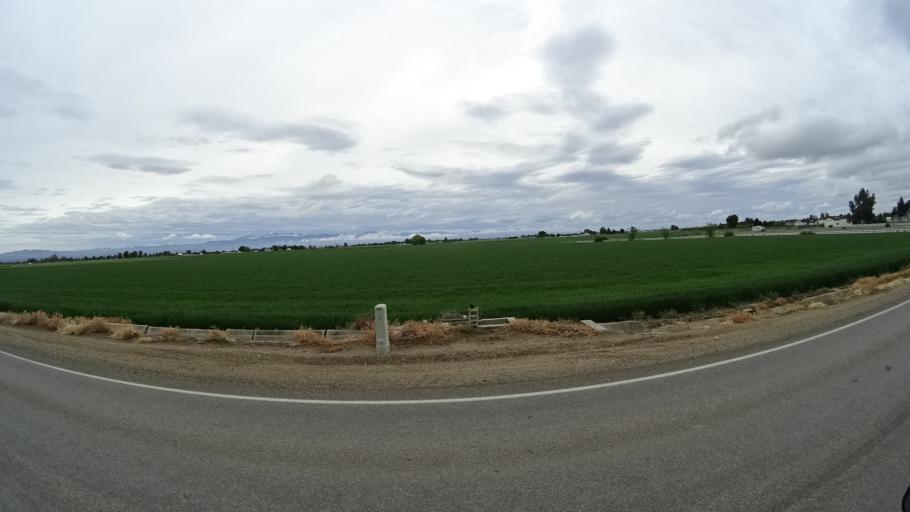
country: US
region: Idaho
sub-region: Ada County
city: Star
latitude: 43.6592
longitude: -116.4937
